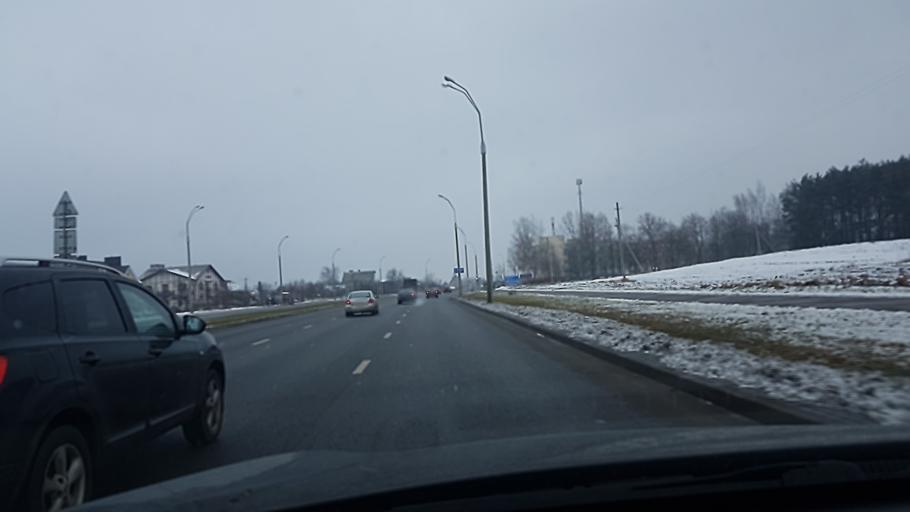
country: BY
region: Minsk
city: Minsk
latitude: 53.9509
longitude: 27.5356
